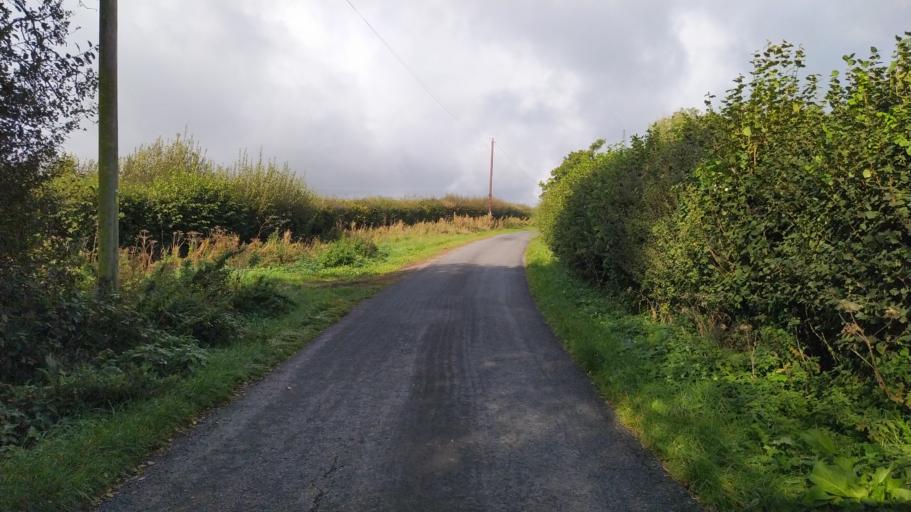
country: GB
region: England
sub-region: Wiltshire
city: Hindon
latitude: 51.0387
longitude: -2.1461
